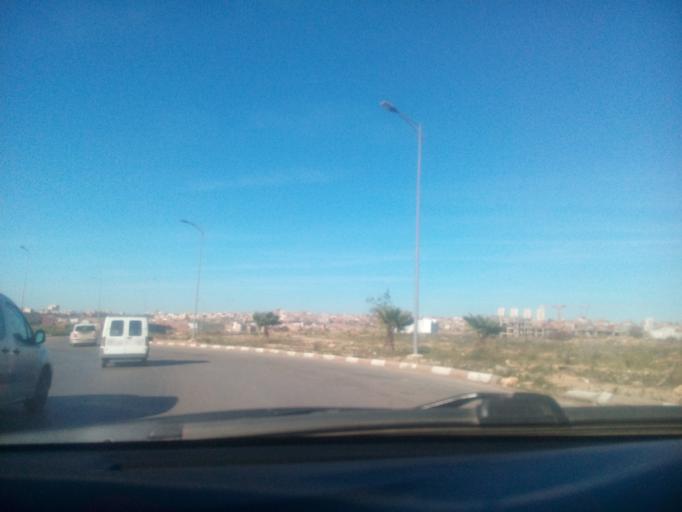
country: DZ
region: Oran
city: Bir el Djir
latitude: 35.7347
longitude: -0.5428
